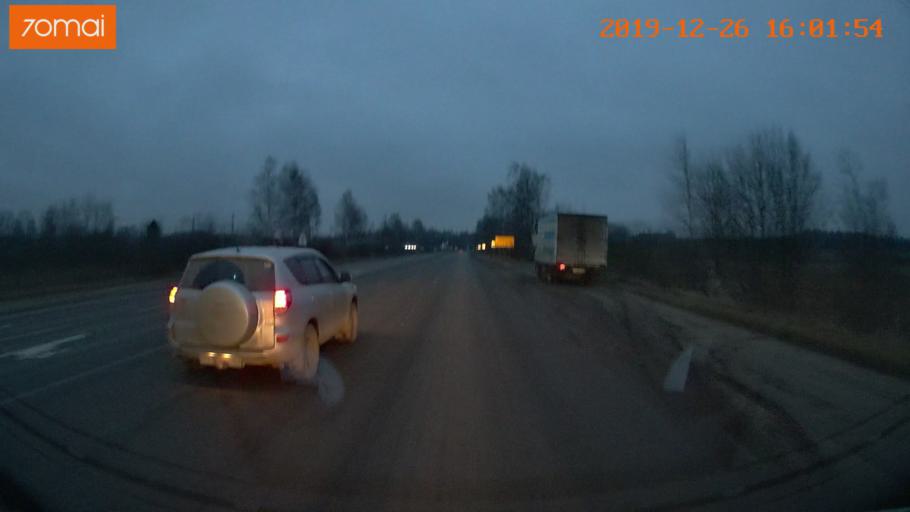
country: RU
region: Jaroslavl
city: Rybinsk
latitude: 58.0151
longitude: 38.8240
